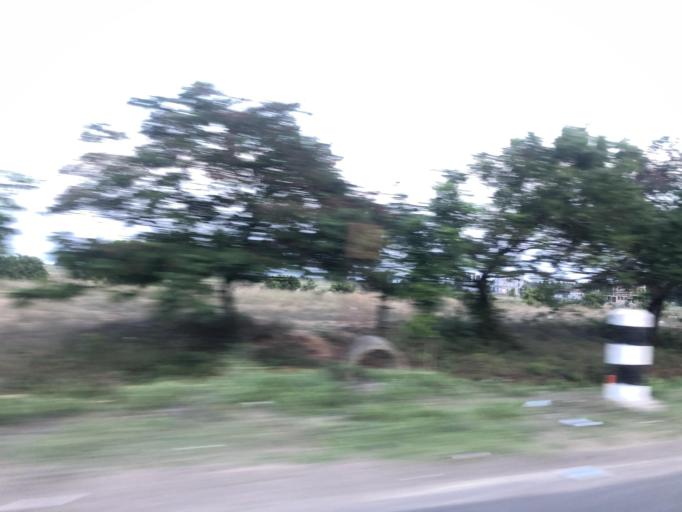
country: IN
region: Tamil Nadu
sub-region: Kancheepuram
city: Mamallapuram
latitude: 12.7510
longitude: 80.2412
